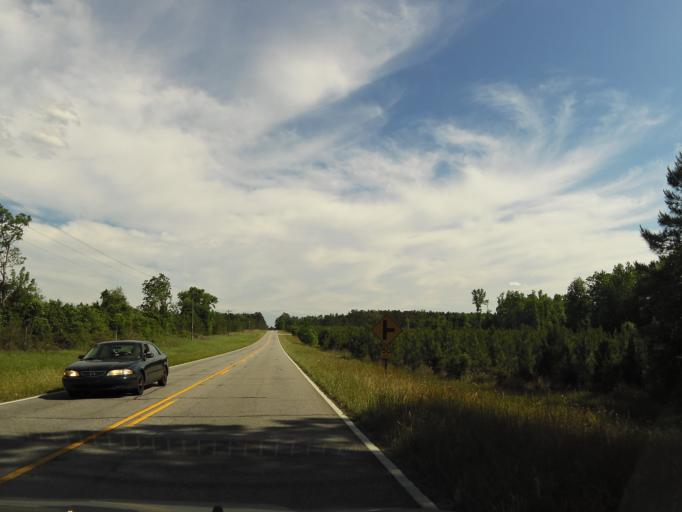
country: US
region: South Carolina
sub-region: Allendale County
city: Allendale
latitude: 33.1347
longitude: -81.1871
